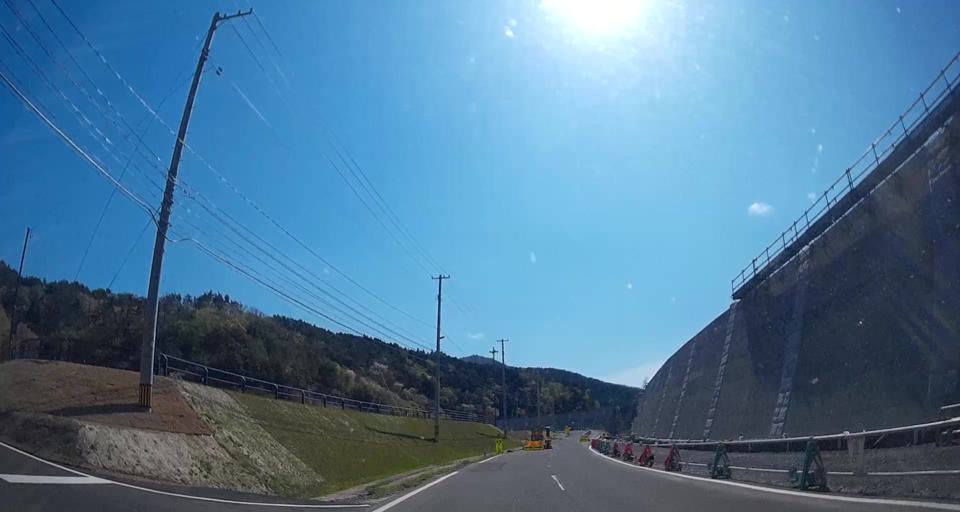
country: JP
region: Miyagi
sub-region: Oshika Gun
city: Onagawa Cho
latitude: 38.5209
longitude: 141.4740
